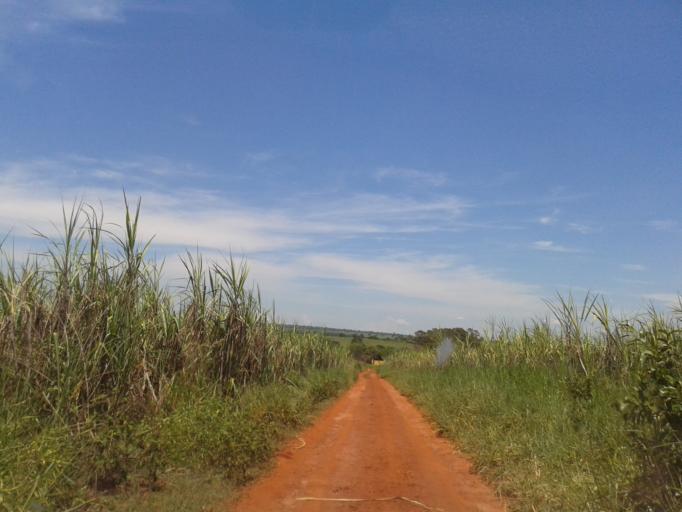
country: BR
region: Minas Gerais
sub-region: Santa Vitoria
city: Santa Vitoria
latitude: -19.1632
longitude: -50.5503
